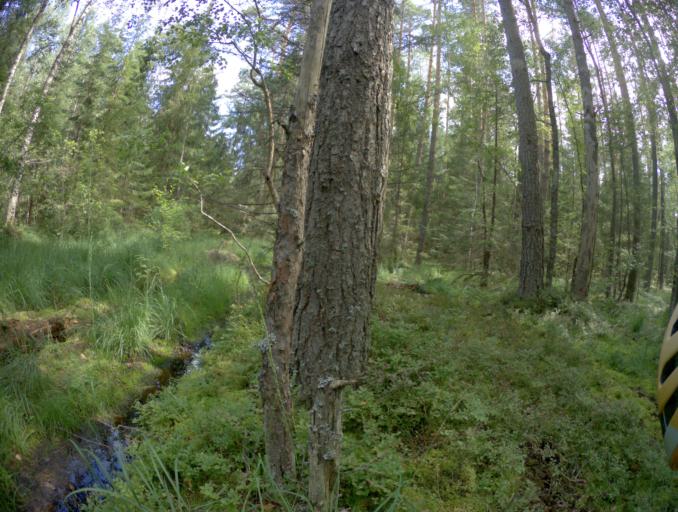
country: RU
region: Vladimir
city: Orgtrud
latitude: 56.0755
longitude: 40.6200
